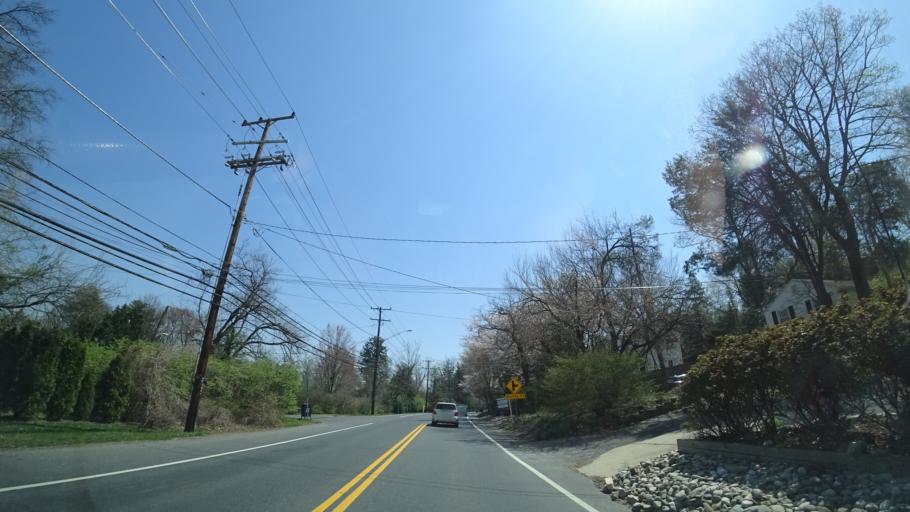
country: US
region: Maryland
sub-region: Montgomery County
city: Bethesda
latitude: 38.9804
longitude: -77.1115
